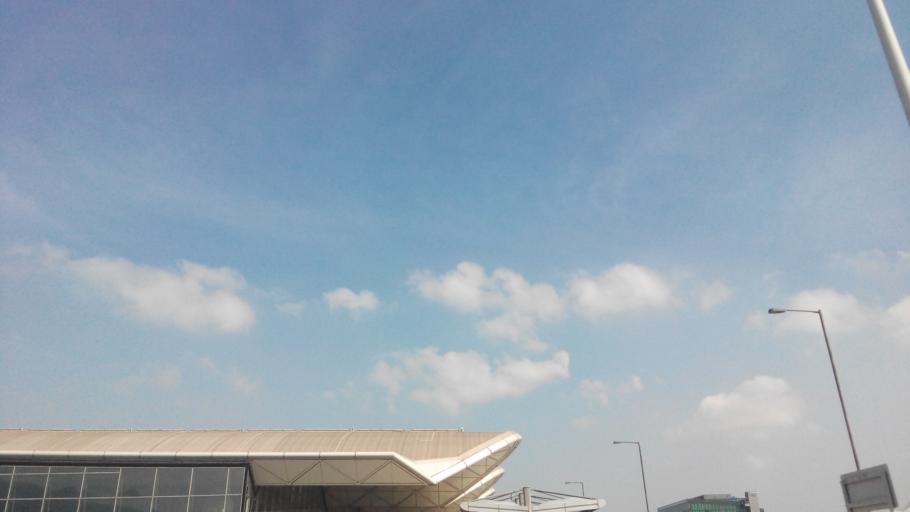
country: HK
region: Tuen Mun
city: Tuen Mun
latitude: 22.3138
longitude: 113.9369
